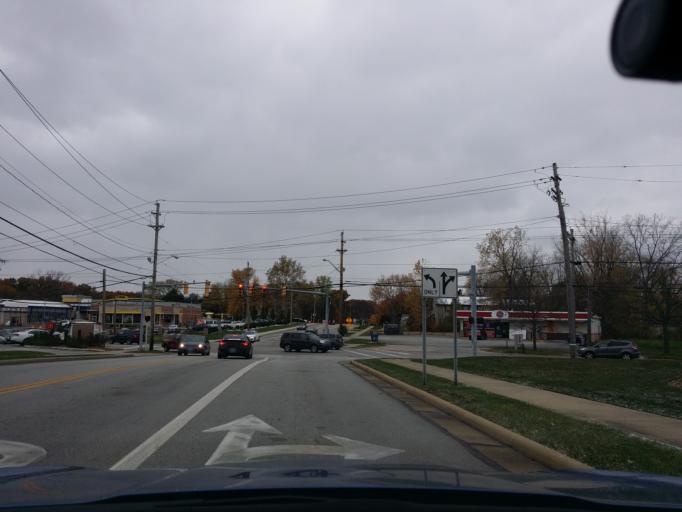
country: US
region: Ohio
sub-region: Cuyahoga County
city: Middleburg Heights
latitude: 41.3430
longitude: -81.8259
